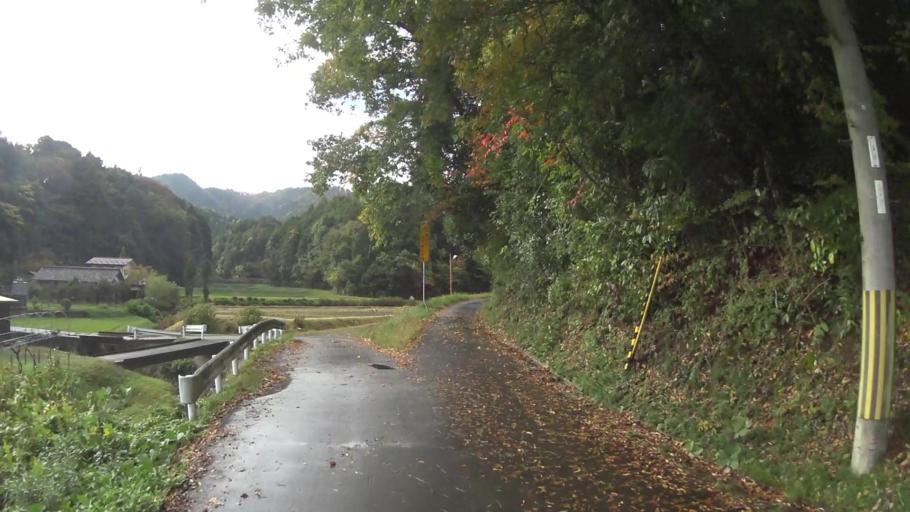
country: JP
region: Kyoto
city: Ayabe
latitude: 35.2780
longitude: 135.2373
